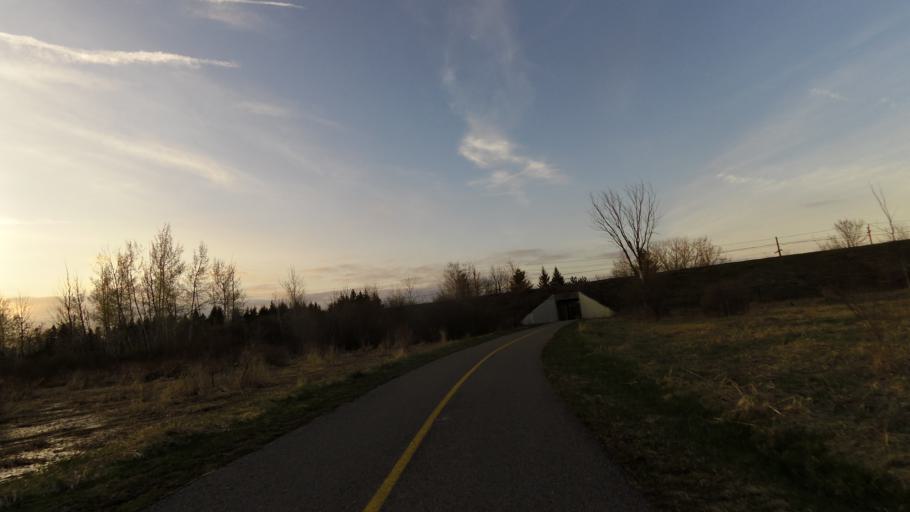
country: CA
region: Ontario
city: Bells Corners
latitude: 45.3430
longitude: -75.8802
